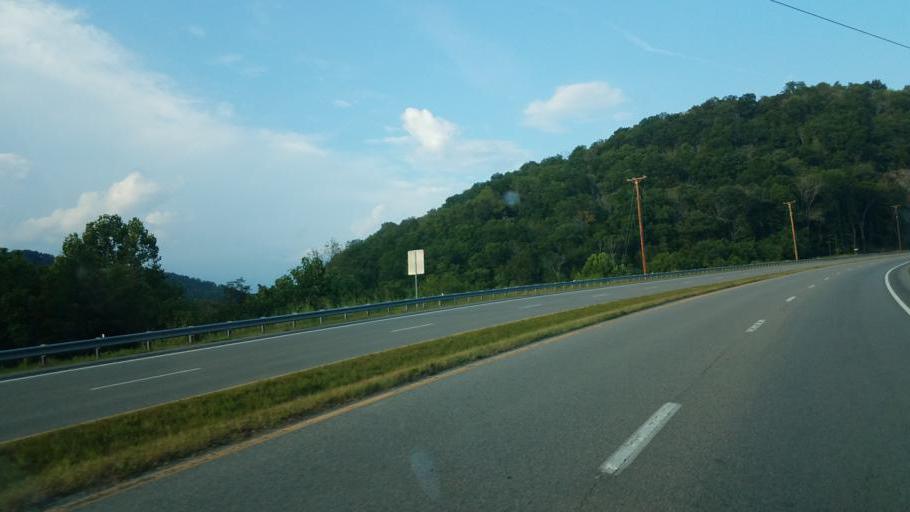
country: US
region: Virginia
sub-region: Lee County
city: Dryden
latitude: 36.7112
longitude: -82.7852
